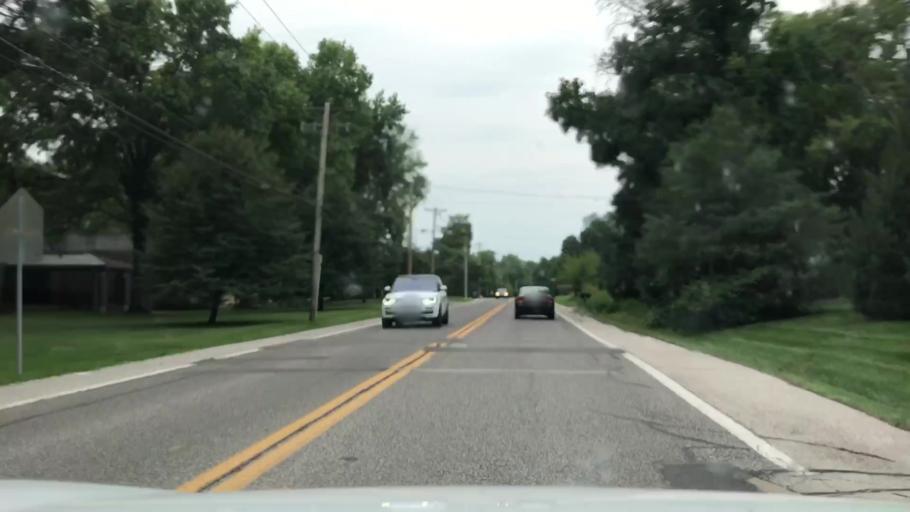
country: US
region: Missouri
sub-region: Saint Louis County
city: Chesterfield
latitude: 38.6566
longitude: -90.5870
